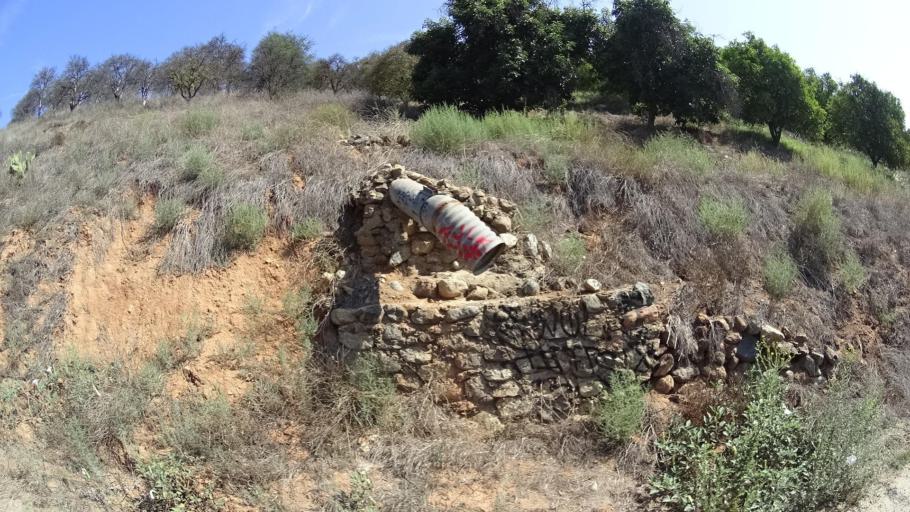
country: US
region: California
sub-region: San Diego County
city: Valley Center
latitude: 33.3217
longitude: -116.9743
